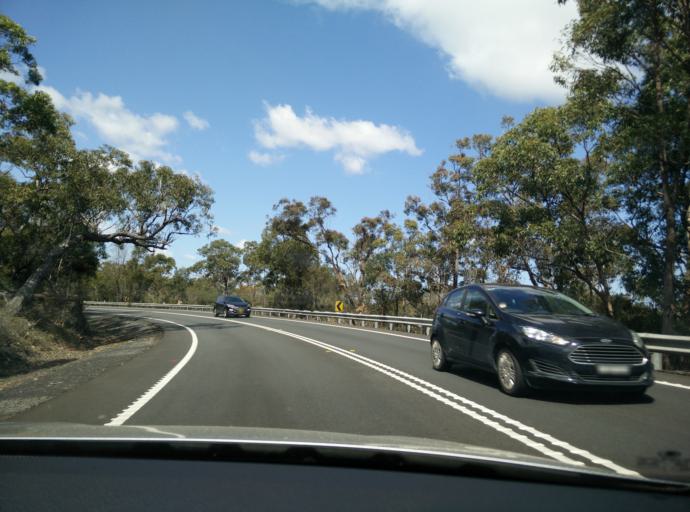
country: AU
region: New South Wales
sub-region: Gosford Shire
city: Point Clare
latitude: -33.4613
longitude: 151.2812
